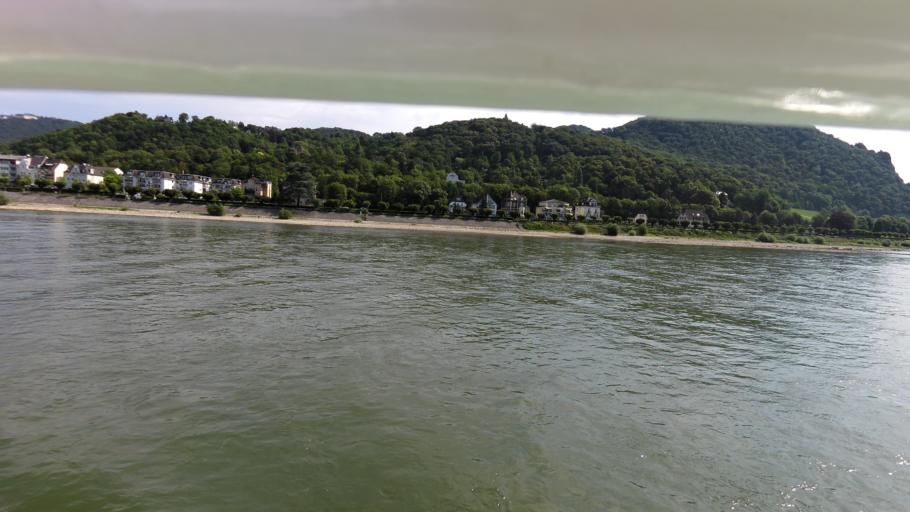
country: DE
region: North Rhine-Westphalia
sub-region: Regierungsbezirk Koln
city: Konigswinter
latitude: 50.6666
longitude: 7.1948
